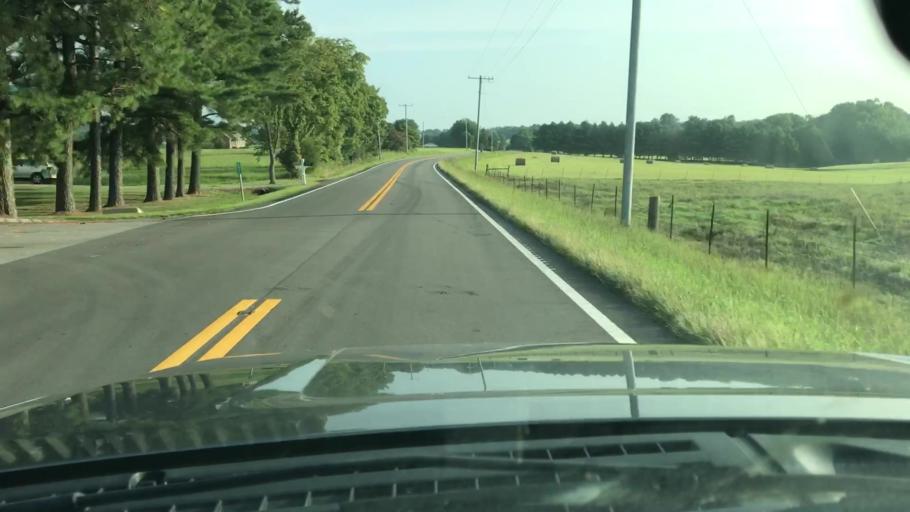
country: US
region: Tennessee
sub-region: Sumner County
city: Portland
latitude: 36.5440
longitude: -86.4101
